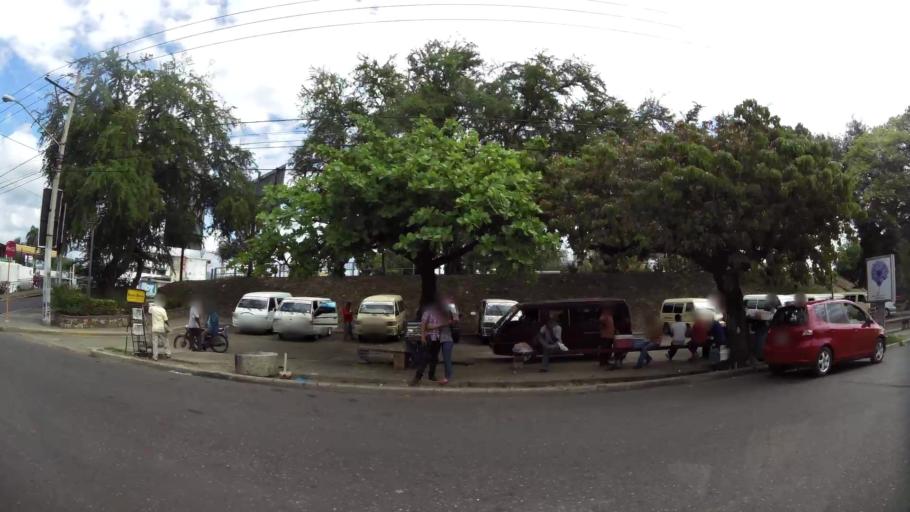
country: DO
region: Santiago
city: Santiago de los Caballeros
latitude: 19.4580
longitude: -70.7092
